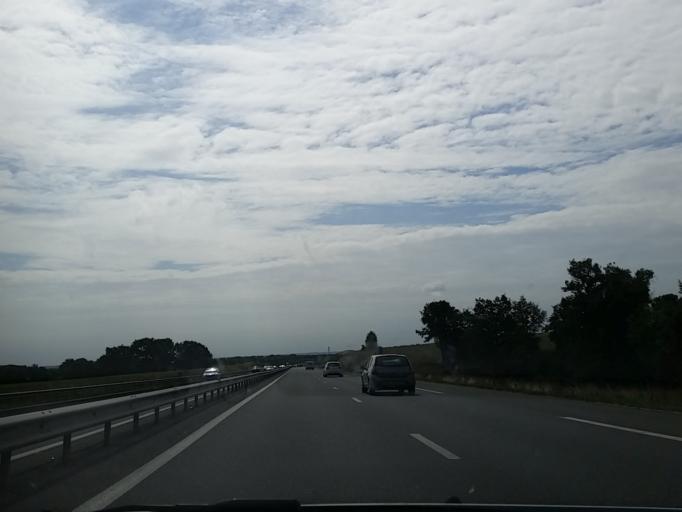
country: FR
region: Auvergne
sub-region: Departement de l'Allier
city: Vallon-en-Sully
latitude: 46.5760
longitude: 2.5304
